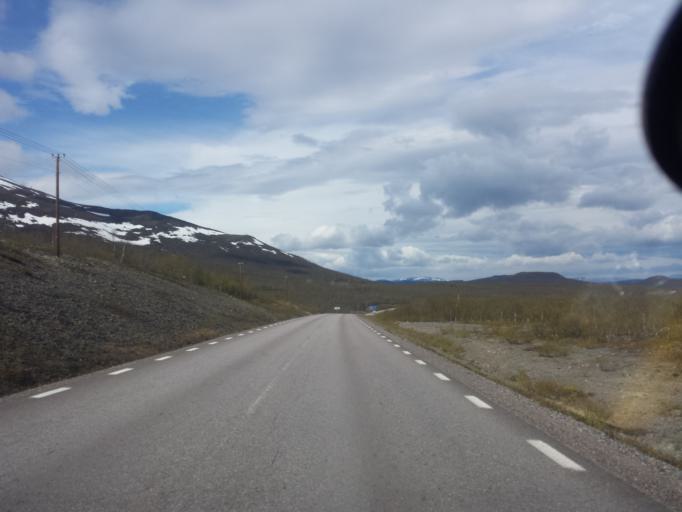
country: SE
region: Norrbotten
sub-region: Kiruna Kommun
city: Kiruna
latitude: 68.1574
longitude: 19.7773
